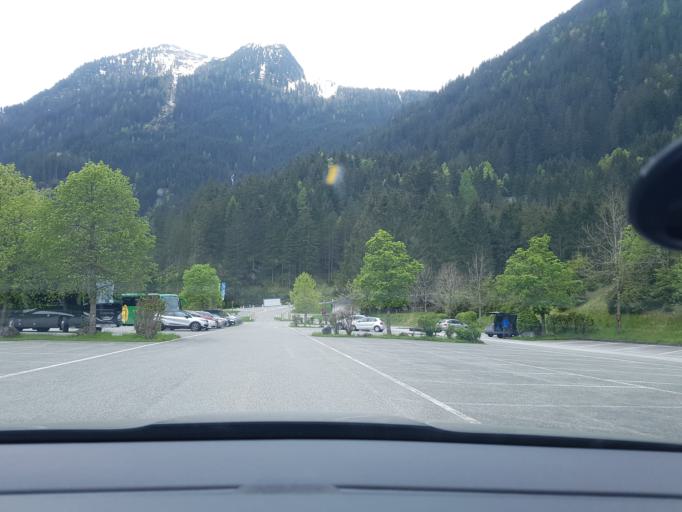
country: AT
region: Salzburg
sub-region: Politischer Bezirk Zell am See
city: Krimml
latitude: 47.2147
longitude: 12.1685
